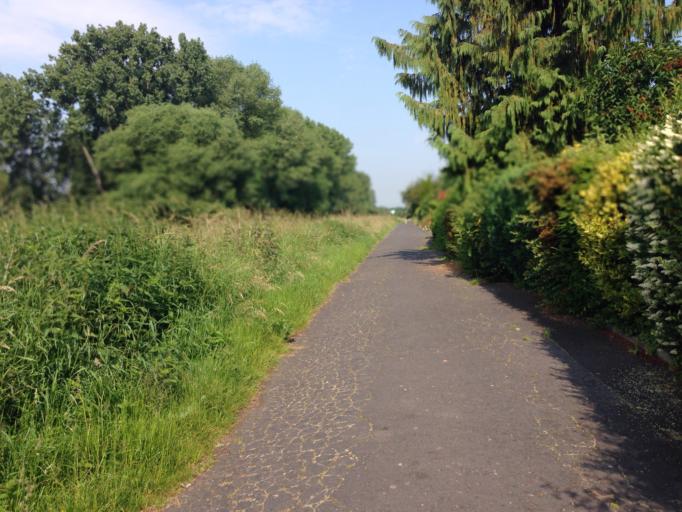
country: DE
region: Hesse
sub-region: Regierungsbezirk Darmstadt
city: Muehlheim am Main
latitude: 50.1319
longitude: 8.8320
